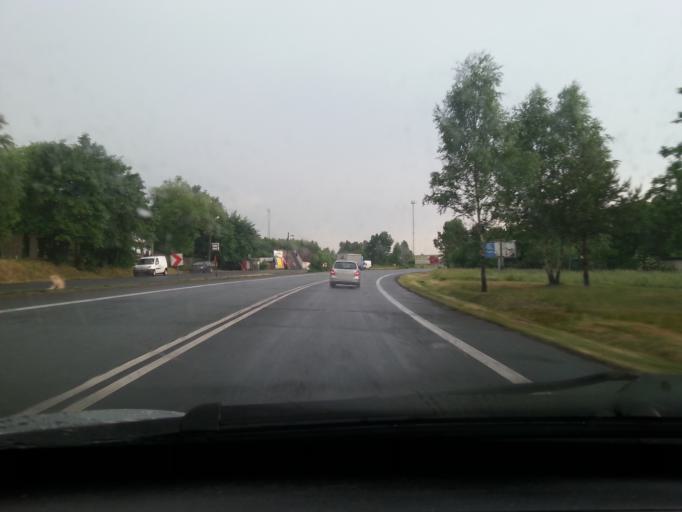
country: PL
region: Lodz Voivodeship
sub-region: Powiat zgierski
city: Strykow
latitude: 51.8428
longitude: 19.5584
